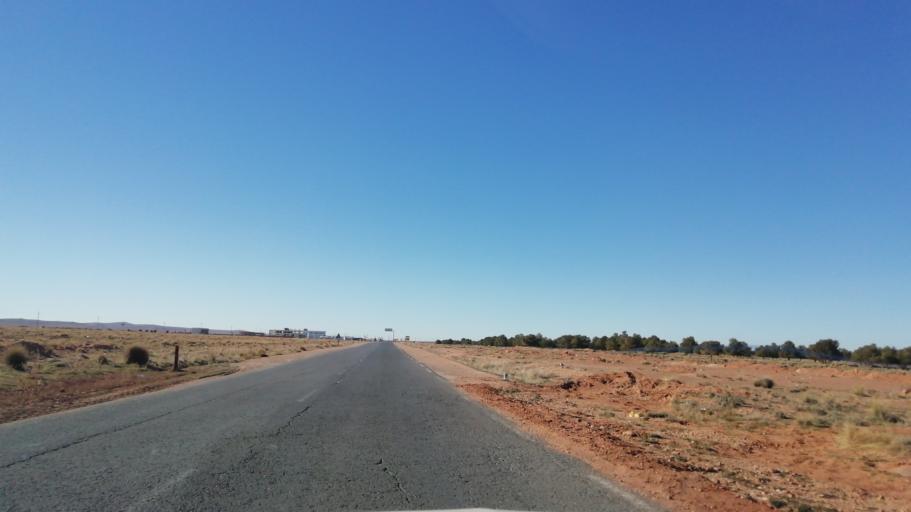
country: DZ
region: El Bayadh
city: El Bayadh
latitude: 33.6609
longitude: 0.9122
